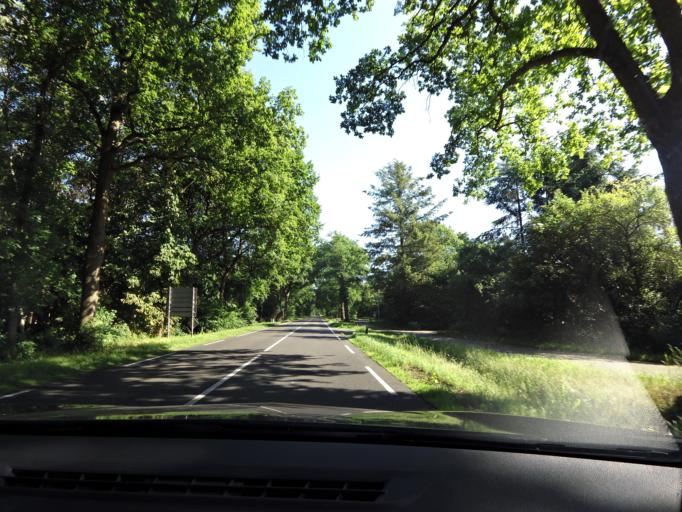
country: NL
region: Overijssel
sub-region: Gemeente Twenterand
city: Den Ham
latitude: 52.4157
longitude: 6.4417
